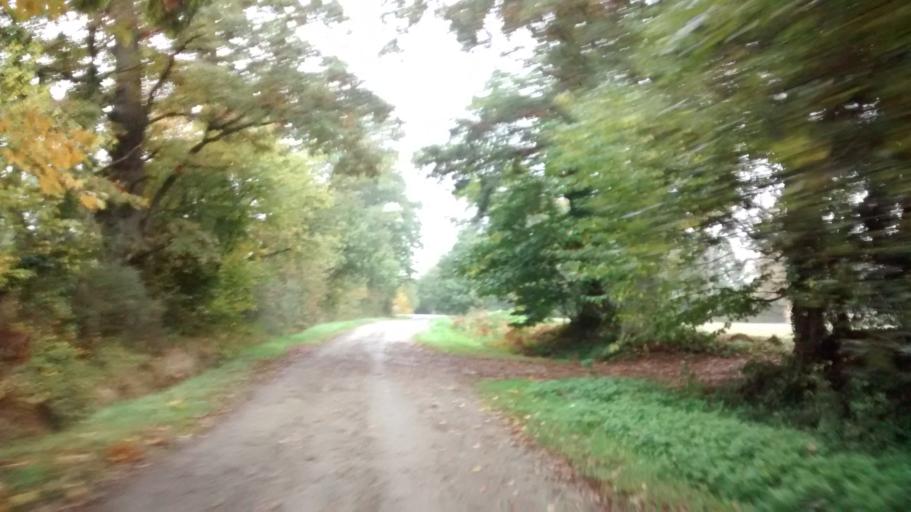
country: FR
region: Brittany
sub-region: Departement d'Ille-et-Vilaine
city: Betton
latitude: 48.1544
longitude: -1.6193
